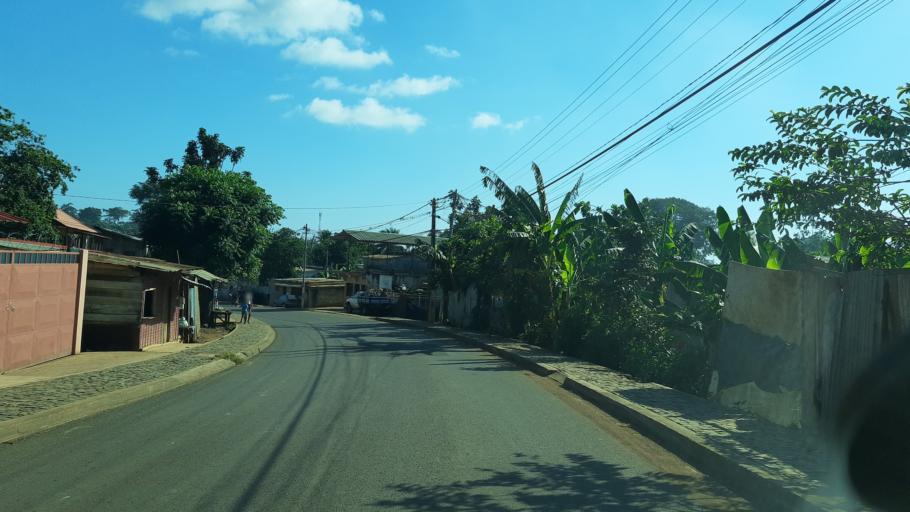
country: ST
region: Sao Tome Island
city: Sao Tome
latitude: 0.3210
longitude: 6.7290
